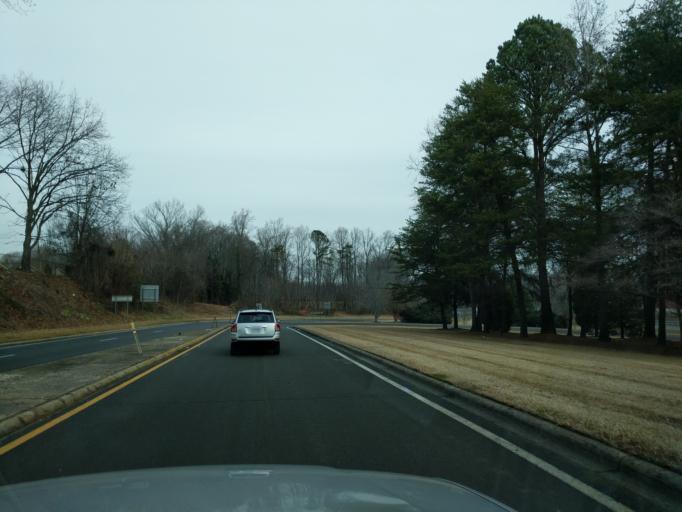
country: US
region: North Carolina
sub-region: Iredell County
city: Statesville
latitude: 35.7917
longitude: -80.8635
